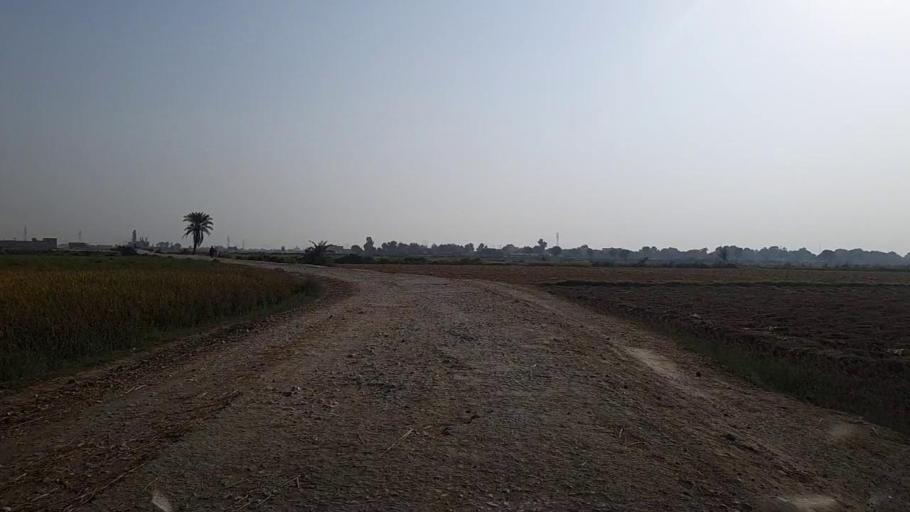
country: PK
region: Sindh
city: Kandhkot
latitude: 28.2825
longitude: 69.2563
